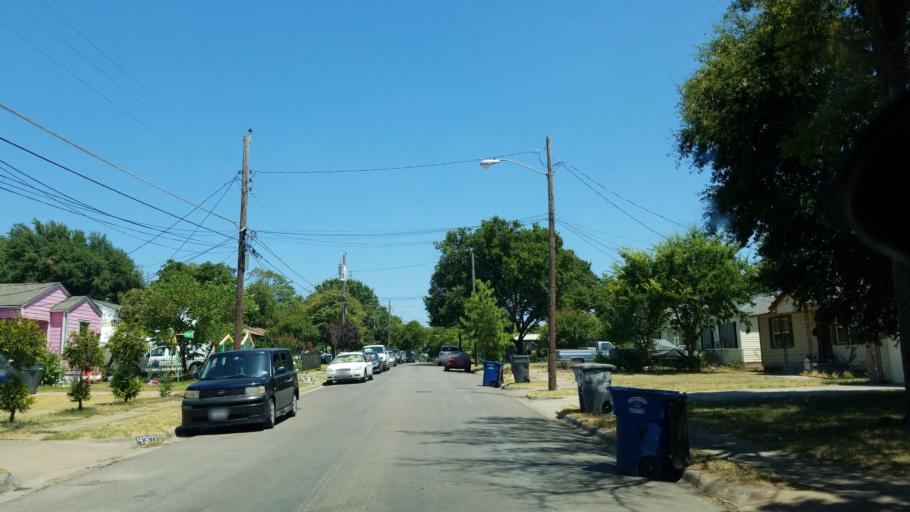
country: US
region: Texas
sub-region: Dallas County
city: Cockrell Hill
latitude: 32.7244
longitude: -96.8901
